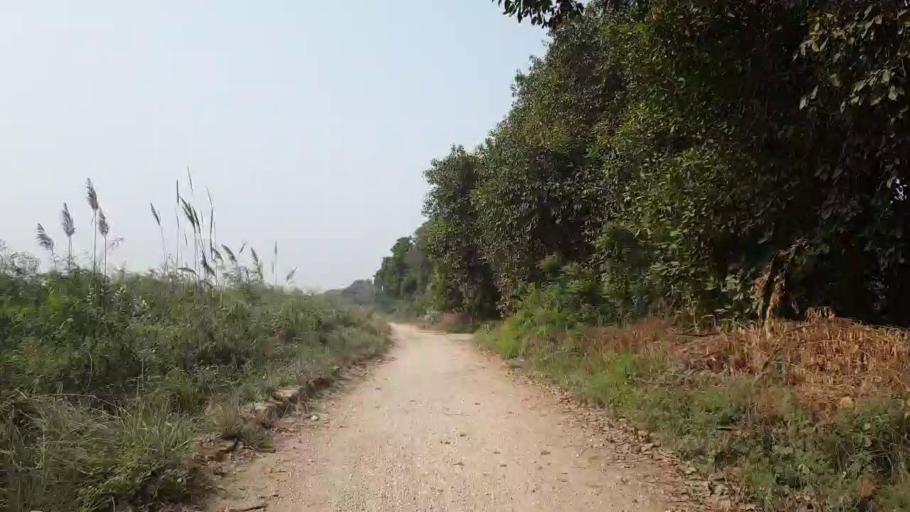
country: PK
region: Sindh
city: Tando Muhammad Khan
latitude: 25.1893
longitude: 68.5938
